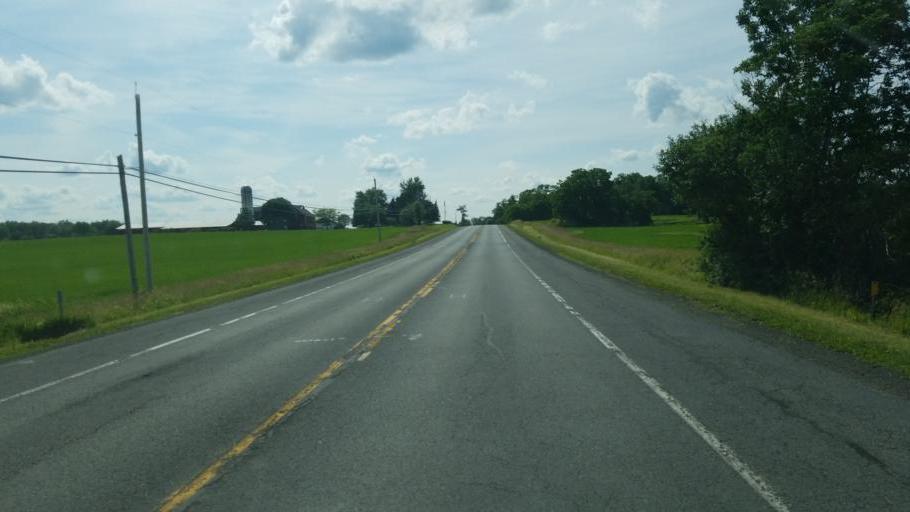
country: US
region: New York
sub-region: Ontario County
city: Shortsville
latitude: 42.8618
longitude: -77.1802
